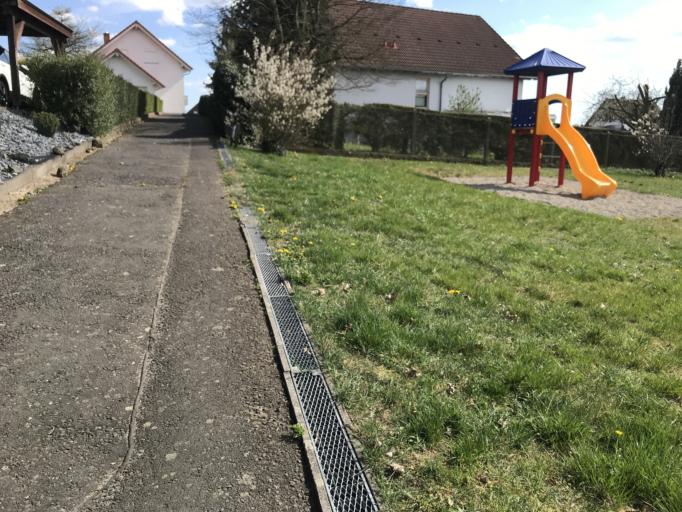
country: DE
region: Hesse
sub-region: Regierungsbezirk Giessen
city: Rabenau
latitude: 50.6935
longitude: 8.8323
